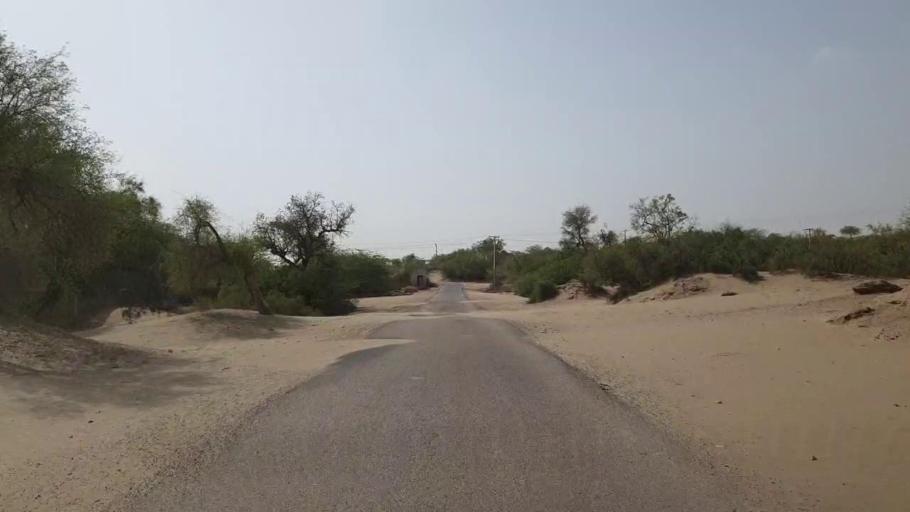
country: PK
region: Sindh
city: Mithi
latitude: 24.5751
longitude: 69.9291
